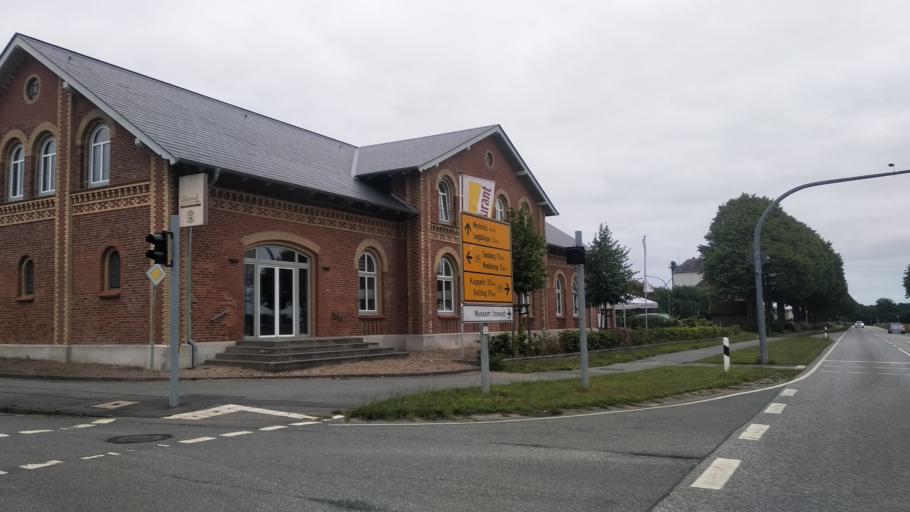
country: DE
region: Schleswig-Holstein
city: Langballig
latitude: 54.7969
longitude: 9.6369
